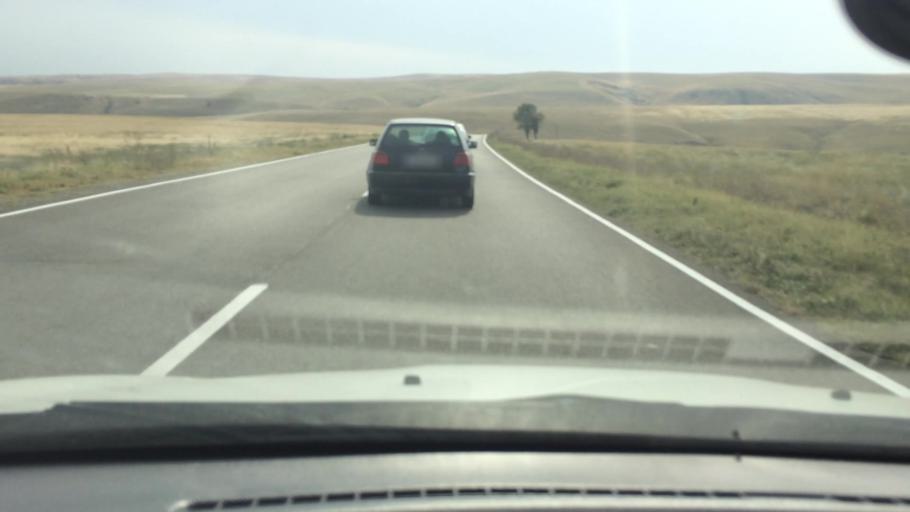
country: GE
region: Kvemo Kartli
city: Rust'avi
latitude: 41.5270
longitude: 44.9379
